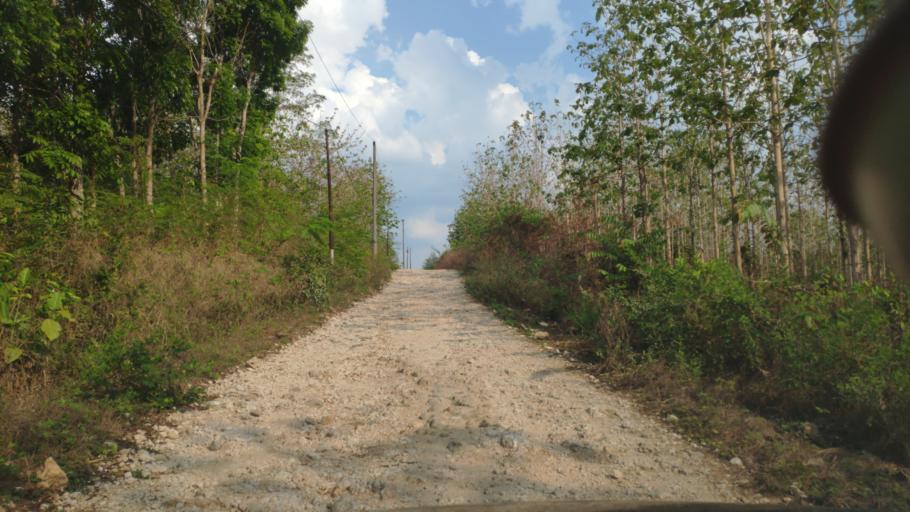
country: ID
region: Central Java
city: Semanggi
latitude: -7.0624
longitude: 111.4155
